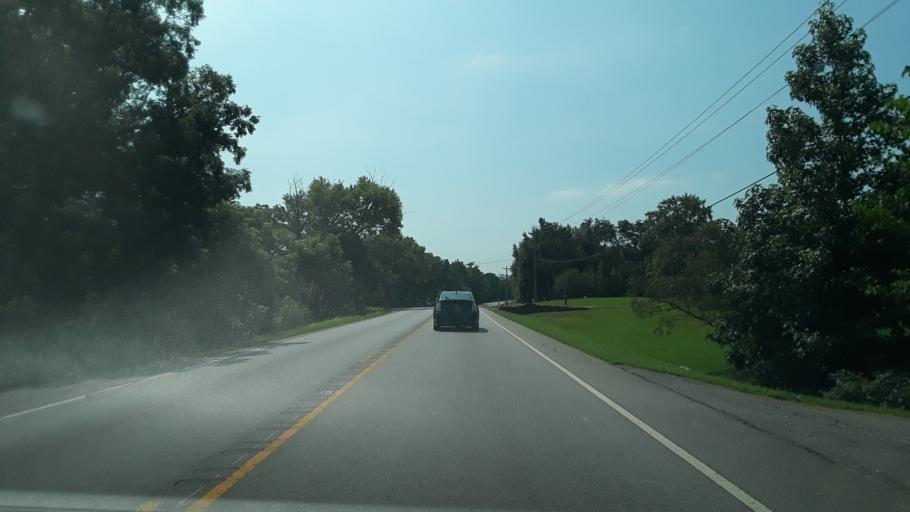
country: US
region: Indiana
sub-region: Clark County
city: Sellersburg
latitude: 38.4354
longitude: -85.8164
